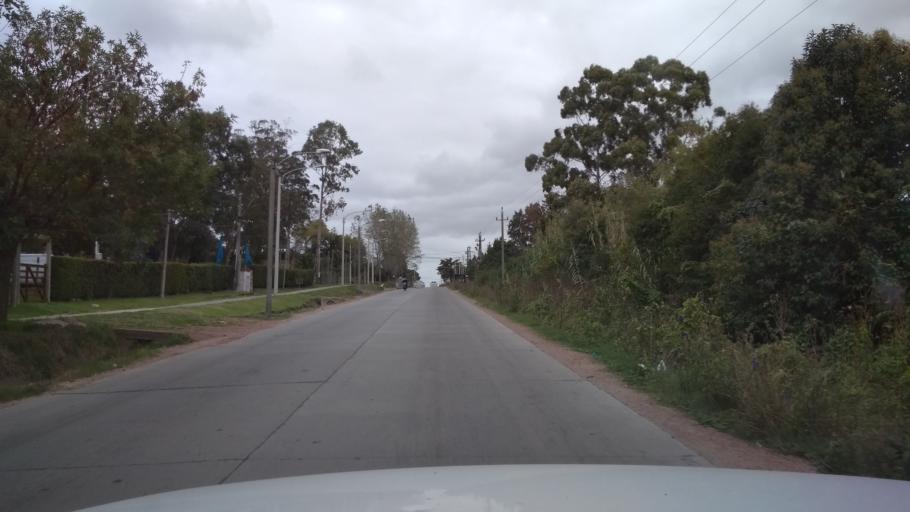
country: UY
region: Canelones
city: Toledo
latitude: -34.7859
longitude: -56.1412
